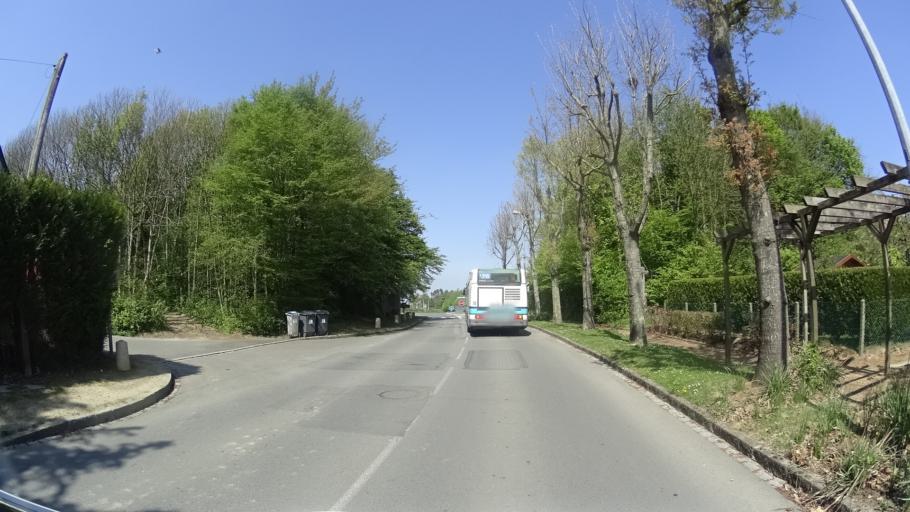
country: FR
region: Brittany
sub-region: Departement d'Ille-et-Vilaine
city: Chavagne
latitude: 48.0586
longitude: -1.7880
